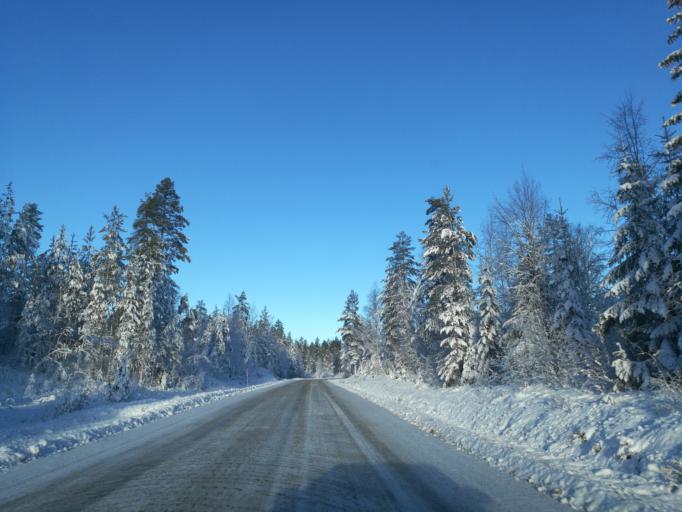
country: NO
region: Hedmark
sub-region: Grue
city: Kirkenaer
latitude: 60.5157
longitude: 12.5531
